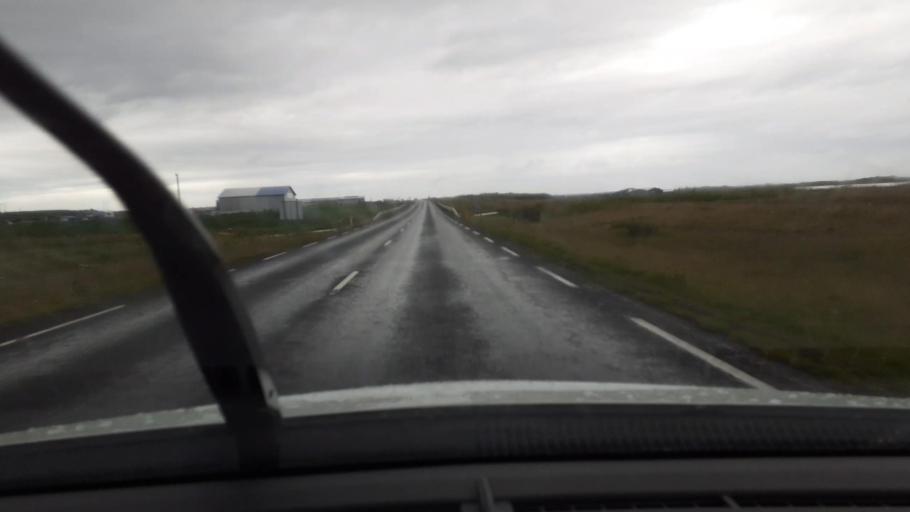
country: IS
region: West
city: Akranes
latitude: 64.3447
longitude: -22.0108
